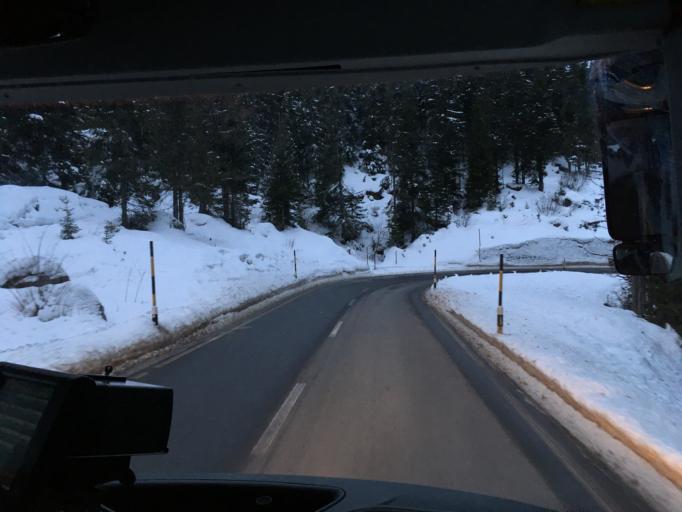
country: CH
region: Grisons
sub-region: Maloja District
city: Silvaplana
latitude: 46.4904
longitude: 9.6429
